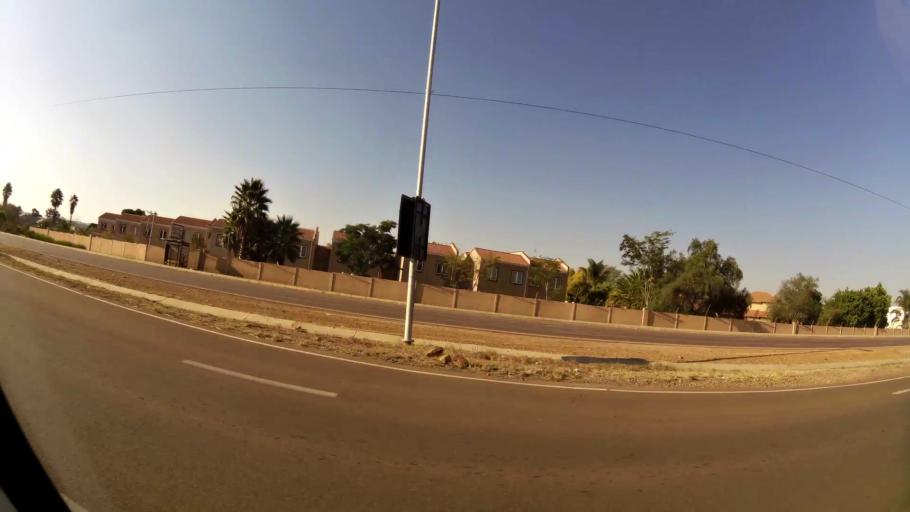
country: ZA
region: Gauteng
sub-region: City of Tshwane Metropolitan Municipality
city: Centurion
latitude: -25.8197
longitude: 28.3059
